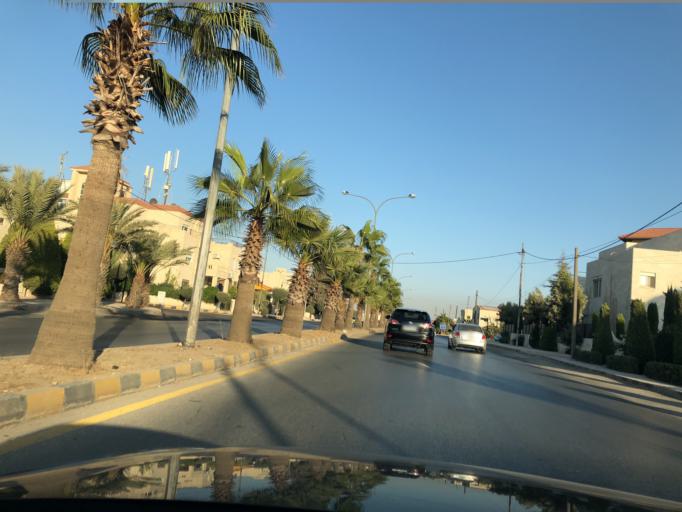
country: JO
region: Amman
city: Al Bunayyat ash Shamaliyah
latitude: 31.9431
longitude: 35.8780
